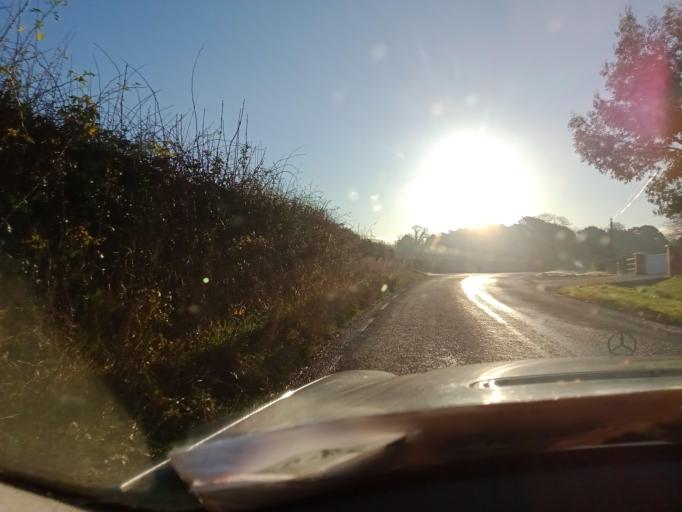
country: IE
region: Leinster
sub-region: Kilkenny
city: Callan
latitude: 52.5298
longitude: -7.3826
